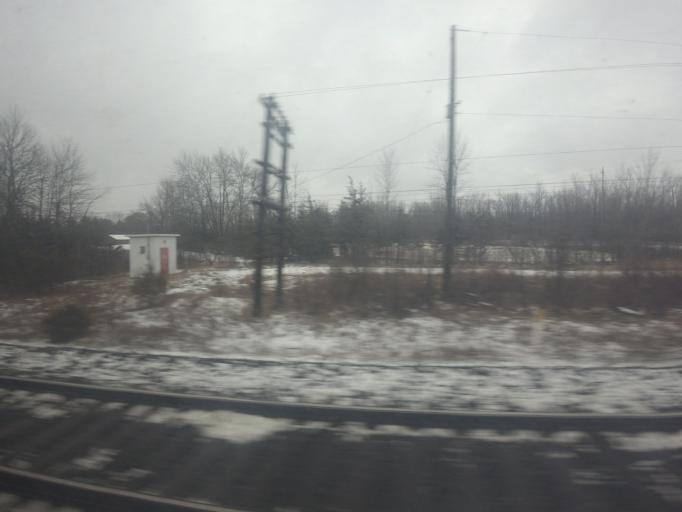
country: CA
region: Ontario
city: Quinte West
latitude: 44.1474
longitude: -77.4924
